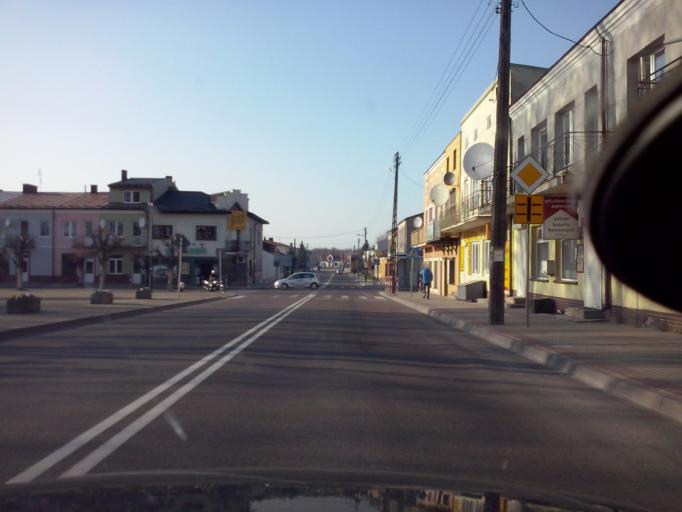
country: PL
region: Lublin Voivodeship
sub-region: Powiat janowski
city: Modliborzyce
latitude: 50.7536
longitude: 22.3297
